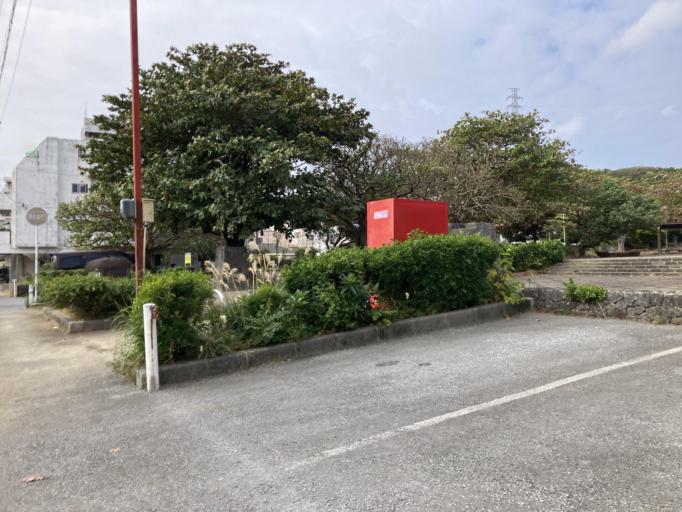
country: JP
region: Okinawa
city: Ginowan
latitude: 26.2075
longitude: 127.7549
